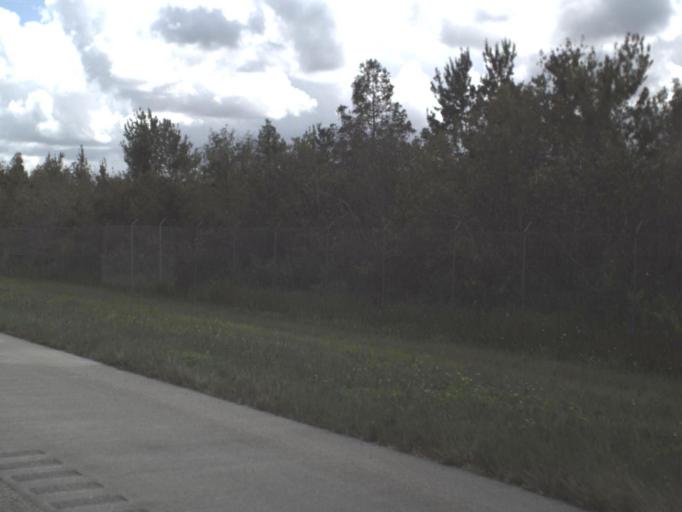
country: US
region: Florida
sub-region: Collier County
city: Orangetree
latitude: 26.1541
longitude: -81.3757
